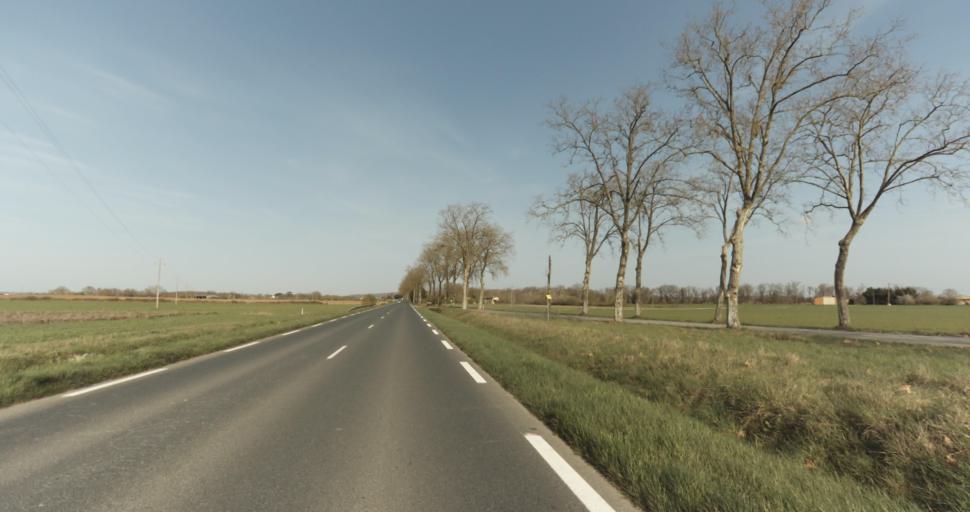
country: FR
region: Midi-Pyrenees
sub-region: Departement du Tarn
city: Saint-Sulpice-la-Pointe
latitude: 43.7550
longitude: 1.7189
